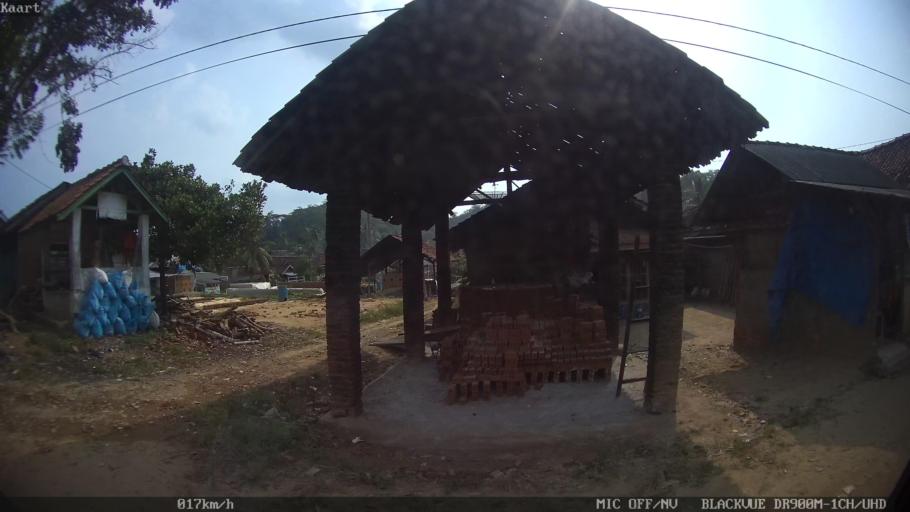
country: ID
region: Lampung
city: Gadingrejo
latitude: -5.3888
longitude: 105.0198
